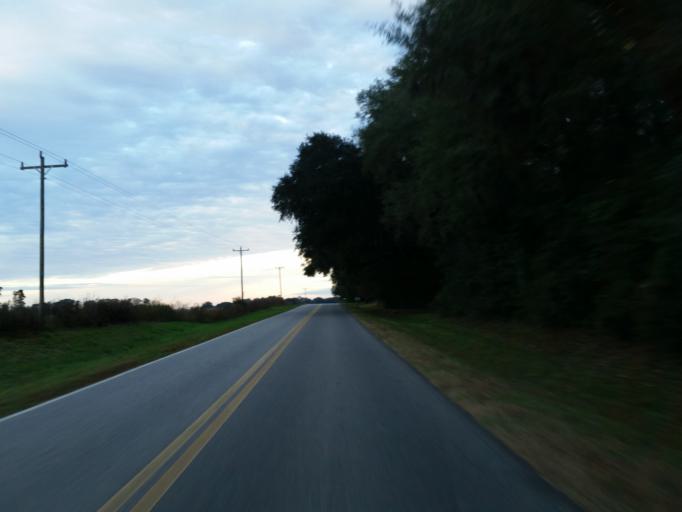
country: US
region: Florida
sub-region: Hamilton County
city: Jasper
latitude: 30.5265
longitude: -83.1016
